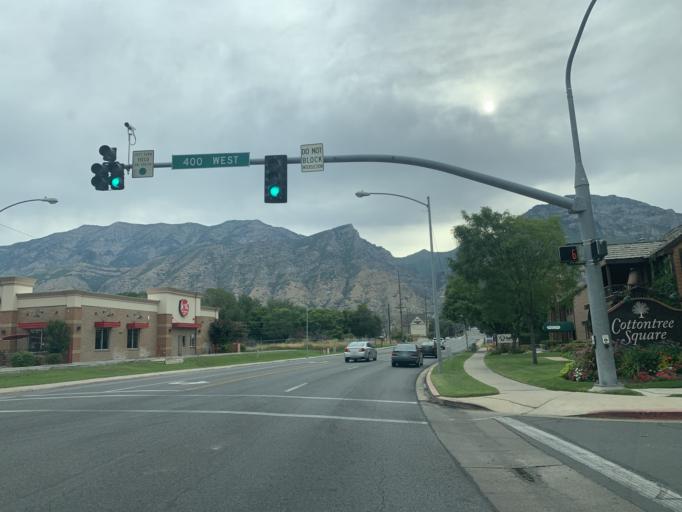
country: US
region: Utah
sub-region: Utah County
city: Provo
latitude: 40.2635
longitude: -111.6663
